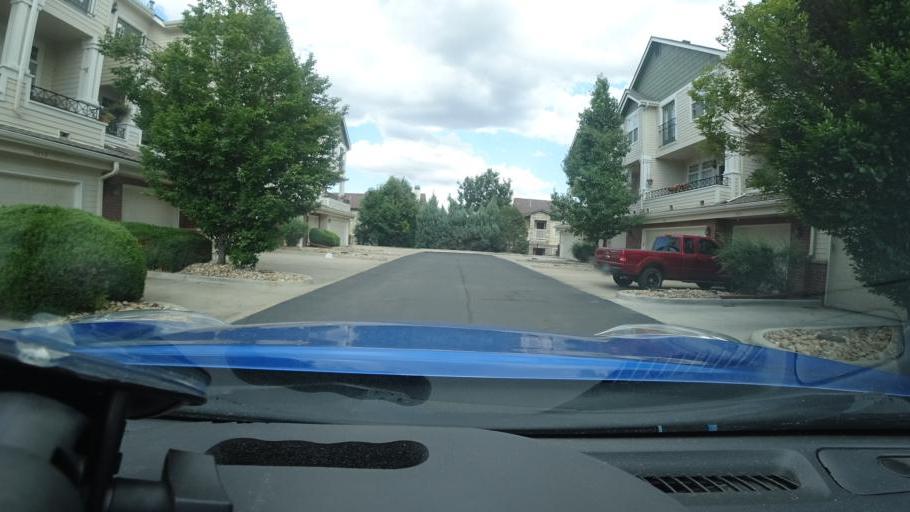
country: US
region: Colorado
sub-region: Adams County
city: Aurora
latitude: 39.6903
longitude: -104.8735
